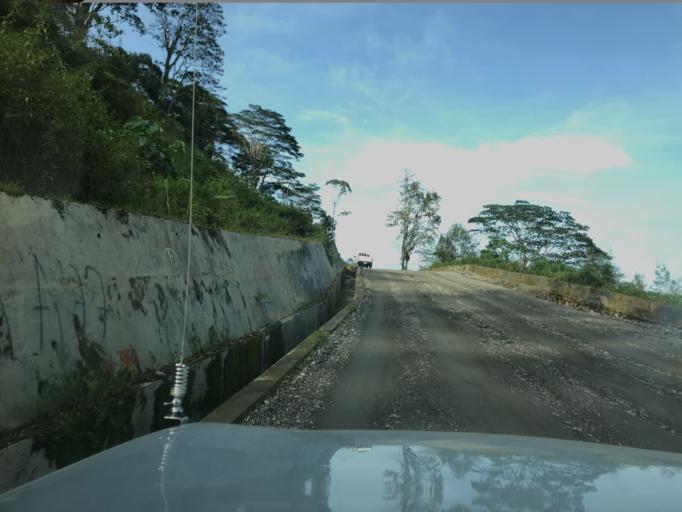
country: TL
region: Aileu
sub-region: Aileu Villa
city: Aileu
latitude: -8.6723
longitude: 125.5519
